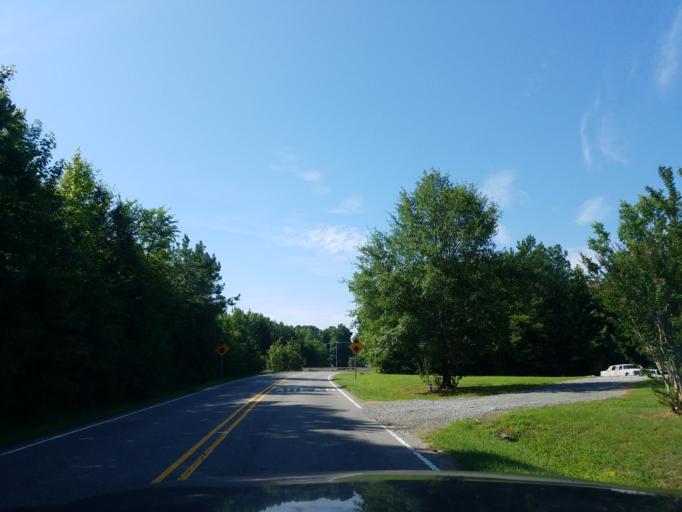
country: US
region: North Carolina
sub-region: Durham County
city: Gorman
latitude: 36.0262
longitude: -78.8411
